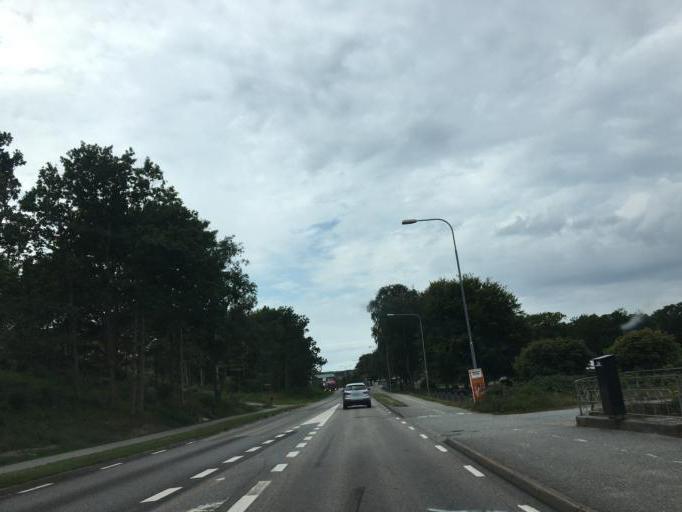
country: SE
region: Vaestra Goetaland
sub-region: Sotenas Kommun
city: Hunnebostrand
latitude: 58.4377
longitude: 11.3023
